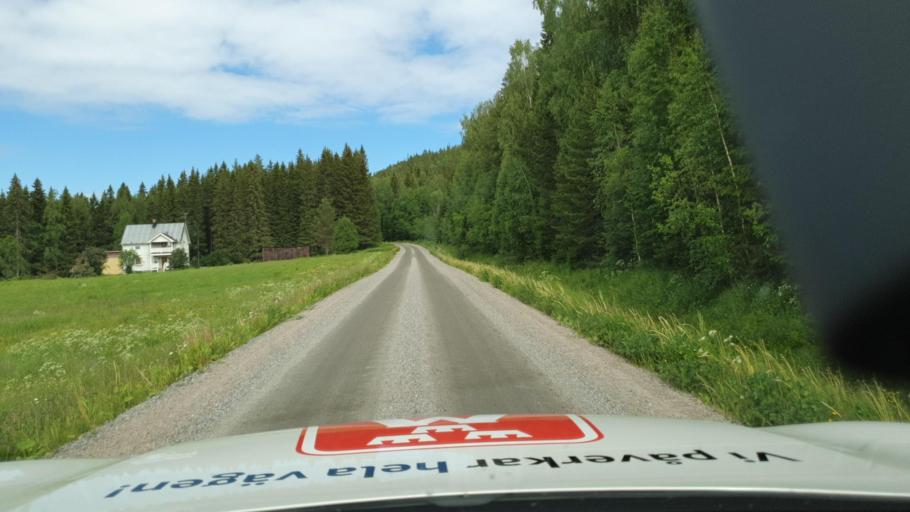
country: SE
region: Vaesterbotten
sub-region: Skelleftea Kommun
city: Forsbacka
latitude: 64.6375
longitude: 20.5455
